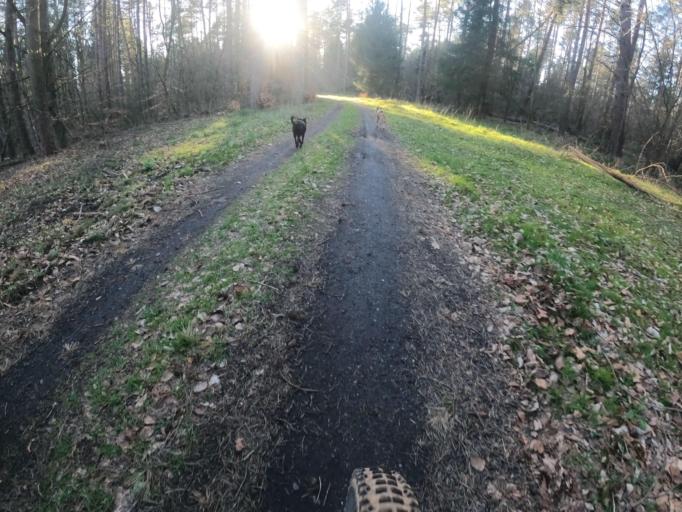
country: PL
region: West Pomeranian Voivodeship
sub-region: Powiat gryficki
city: Brojce
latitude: 53.9570
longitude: 15.3983
